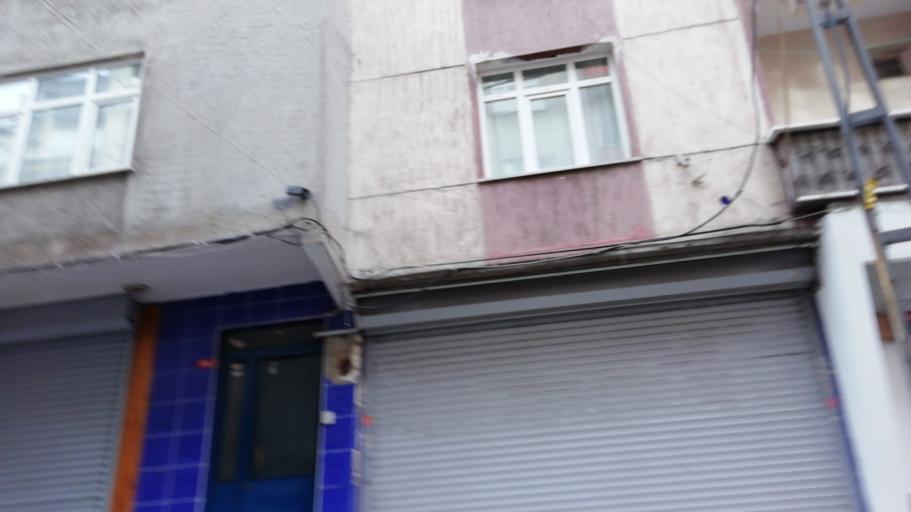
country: TR
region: Istanbul
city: Bagcilar
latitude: 41.0298
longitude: 28.8394
